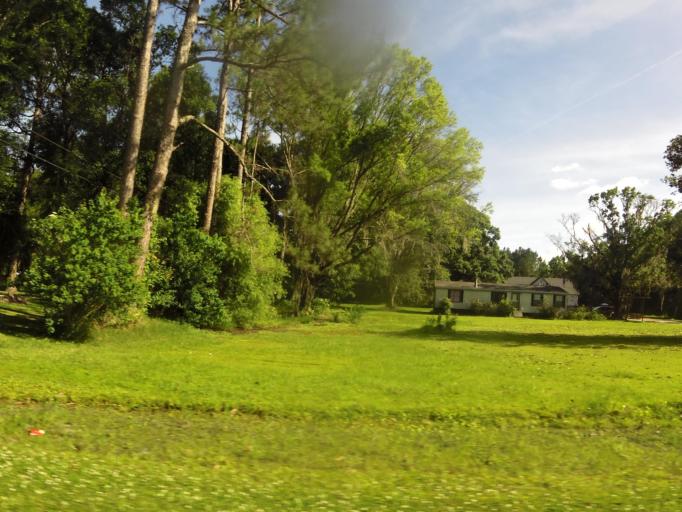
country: US
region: Florida
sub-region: Nassau County
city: Callahan
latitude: 30.5622
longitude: -81.8071
